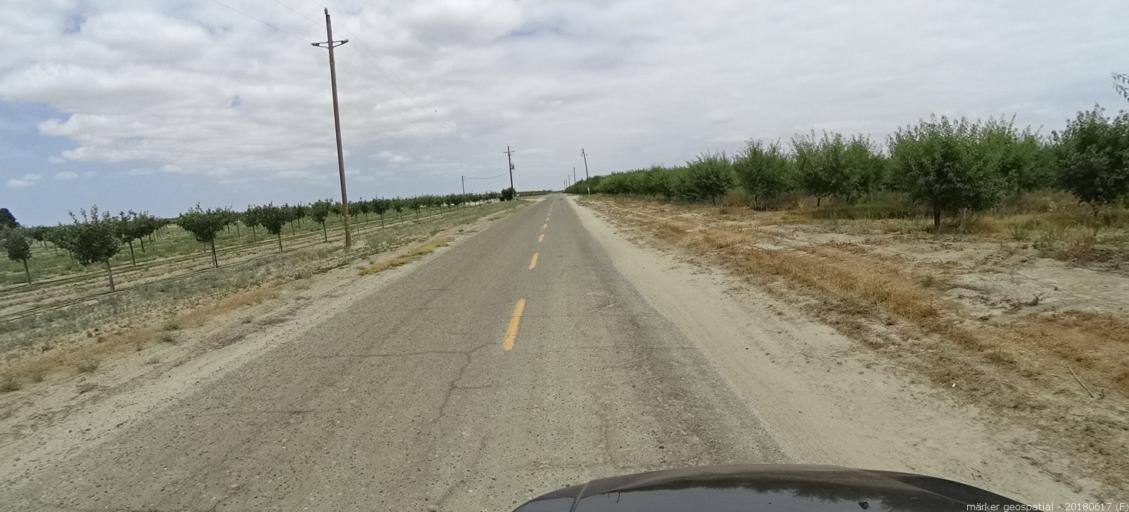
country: US
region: California
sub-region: Fresno County
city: Kerman
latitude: 36.8172
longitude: -120.1870
